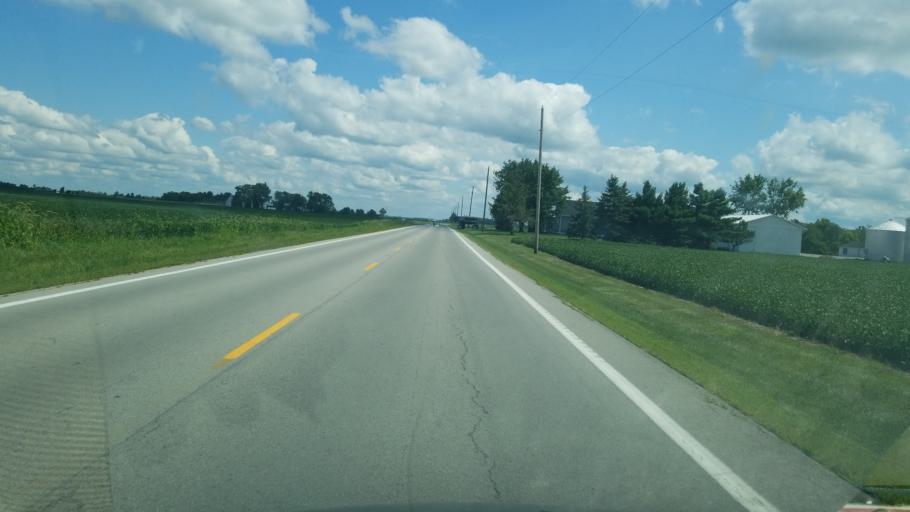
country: US
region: Ohio
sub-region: Putnam County
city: Kalida
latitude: 40.9580
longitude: -84.1774
